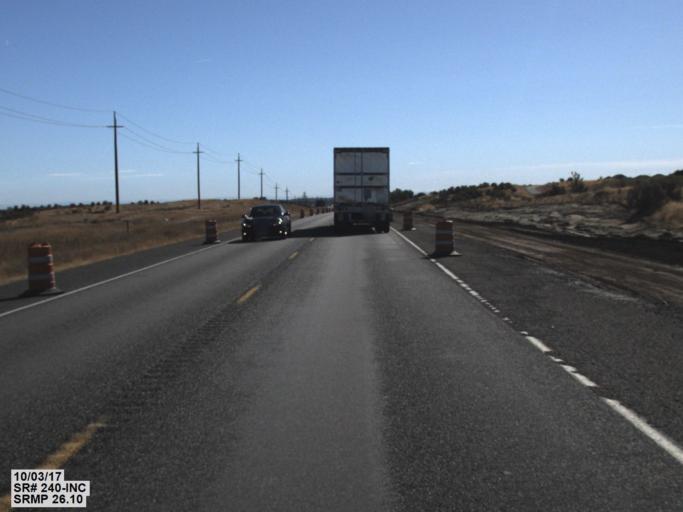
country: US
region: Washington
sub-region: Benton County
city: West Richland
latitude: 46.3328
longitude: -119.3303
